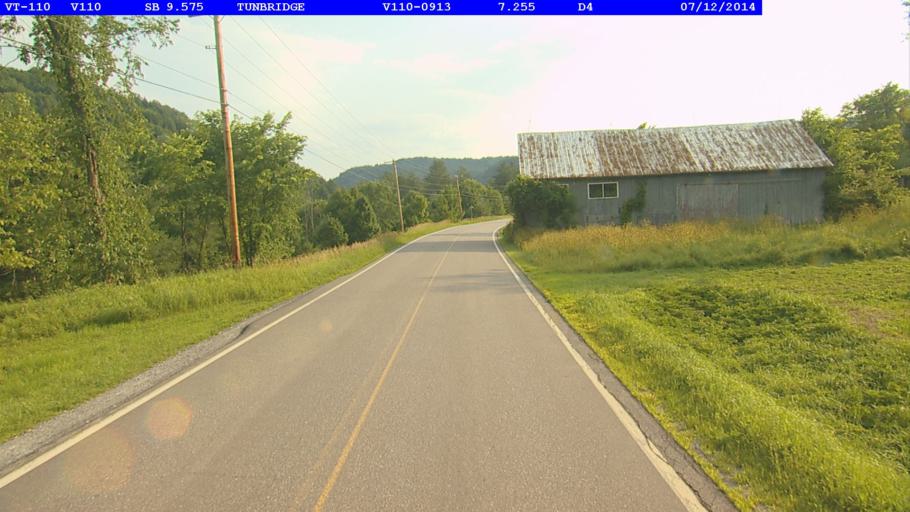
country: US
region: Vermont
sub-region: Orange County
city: Chelsea
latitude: 43.9424
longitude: -72.4623
